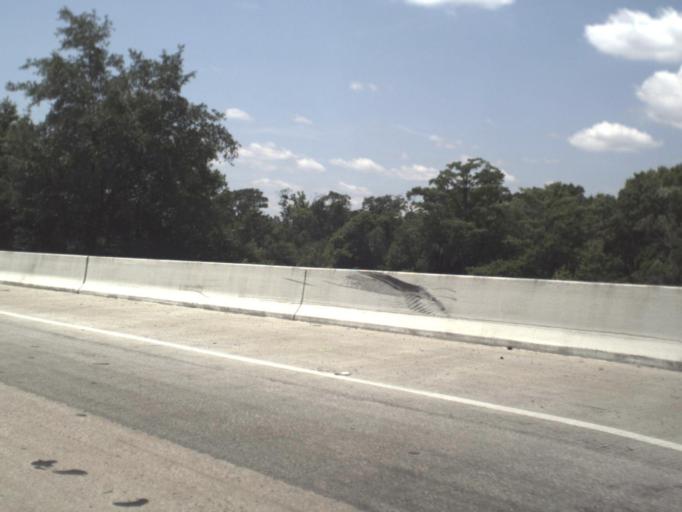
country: US
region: Florida
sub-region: Duval County
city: Jacksonville
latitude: 30.3804
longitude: -81.6737
